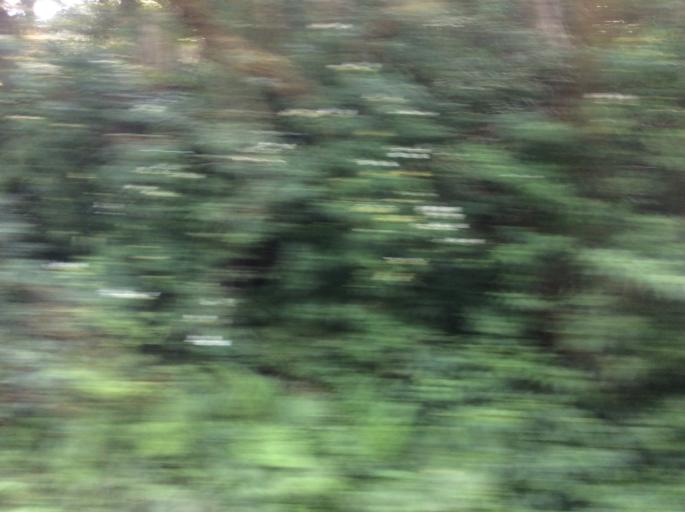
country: TW
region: Taipei
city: Taipei
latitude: 25.1460
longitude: 121.5498
